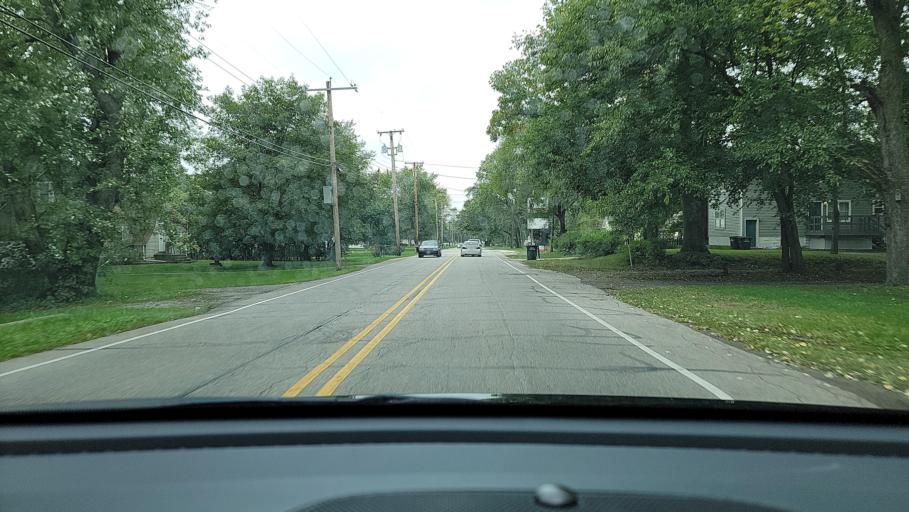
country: US
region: Indiana
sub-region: Lake County
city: Lake Station
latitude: 41.5750
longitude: -87.2150
